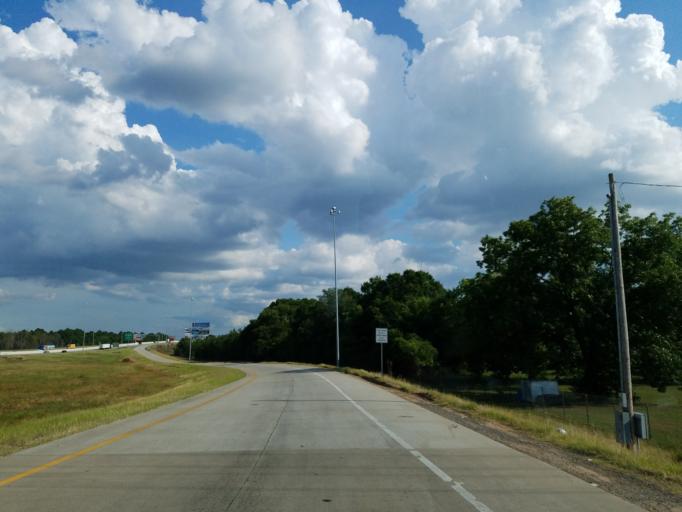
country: US
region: Georgia
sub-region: Crisp County
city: Cordele
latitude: 31.9747
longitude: -83.7555
